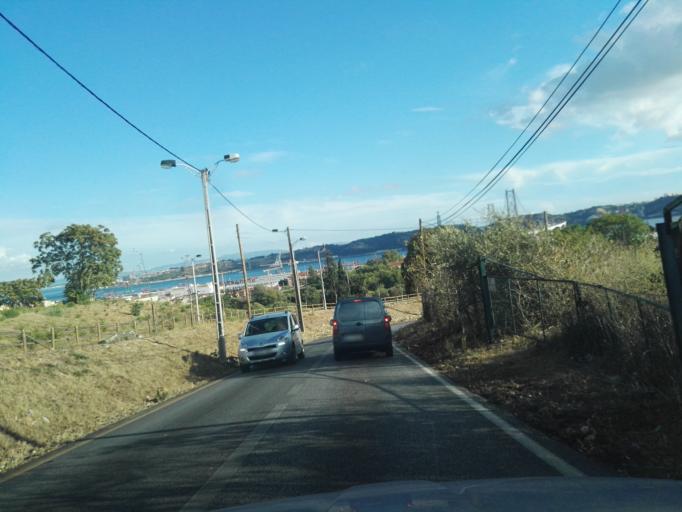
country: PT
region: Setubal
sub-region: Almada
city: Pragal
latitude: 38.7125
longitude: -9.1798
